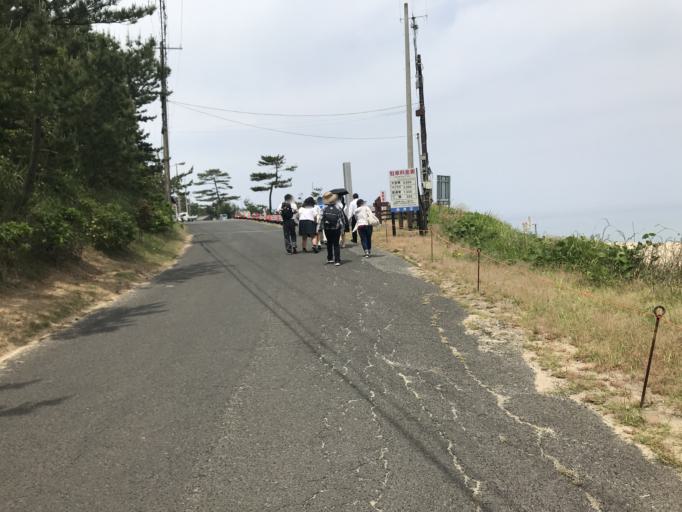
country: JP
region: Kyoto
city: Miyazu
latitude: 35.7017
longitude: 135.0511
